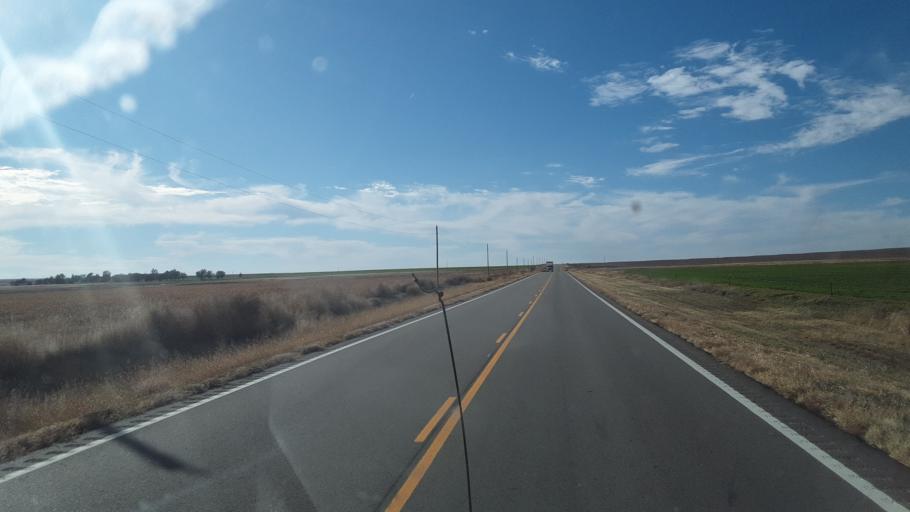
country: US
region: Kansas
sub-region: Hodgeman County
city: Jetmore
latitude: 38.0727
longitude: -100.0198
